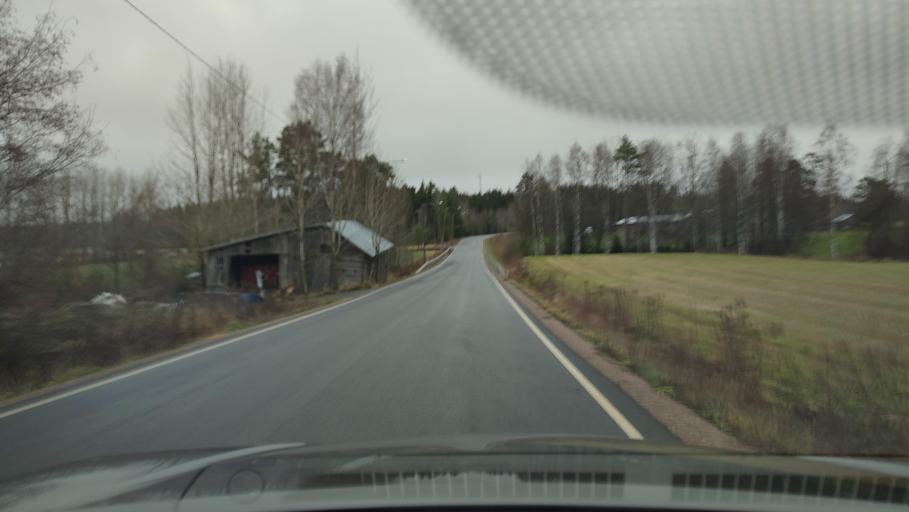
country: FI
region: Southern Ostrobothnia
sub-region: Suupohja
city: Karijoki
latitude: 62.1427
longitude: 21.6865
